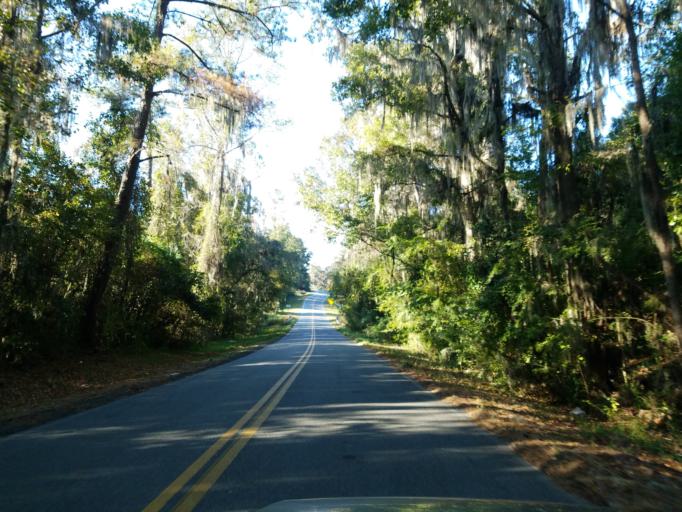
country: US
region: Georgia
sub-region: Echols County
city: Statenville
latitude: 30.6207
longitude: -83.0974
